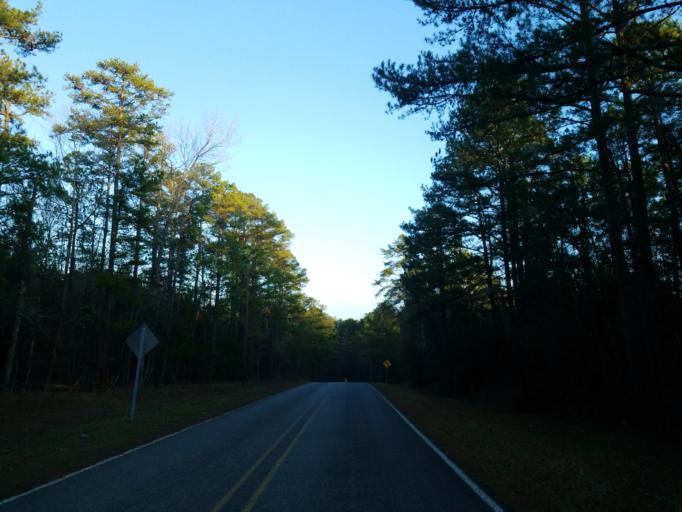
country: US
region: Mississippi
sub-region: Clarke County
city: Stonewall
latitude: 32.2634
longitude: -88.7983
